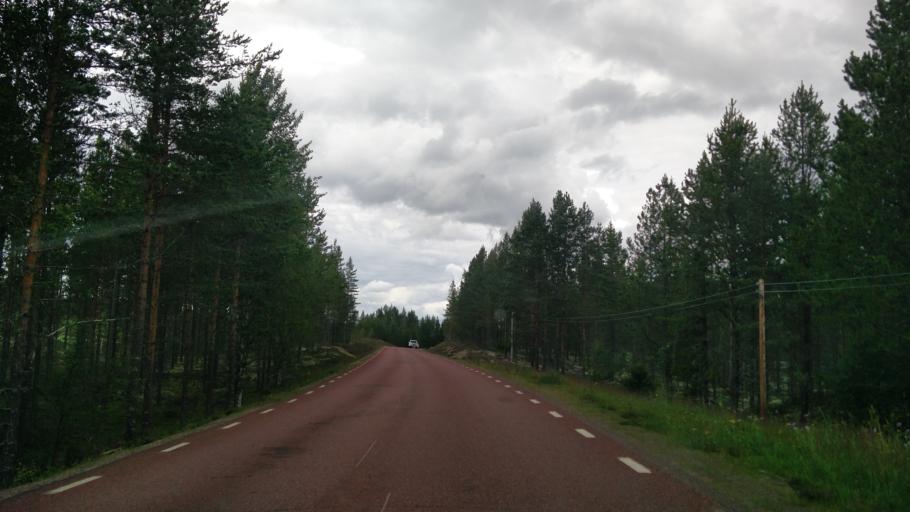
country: NO
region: Hedmark
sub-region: Trysil
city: Innbygda
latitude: 61.1453
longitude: 12.8057
